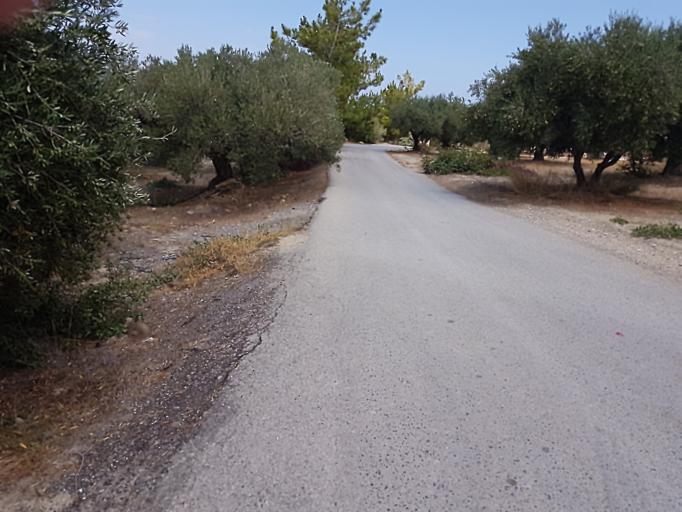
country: GR
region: Crete
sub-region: Nomos Irakleiou
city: Limin Khersonisou
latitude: 35.3098
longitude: 25.3764
